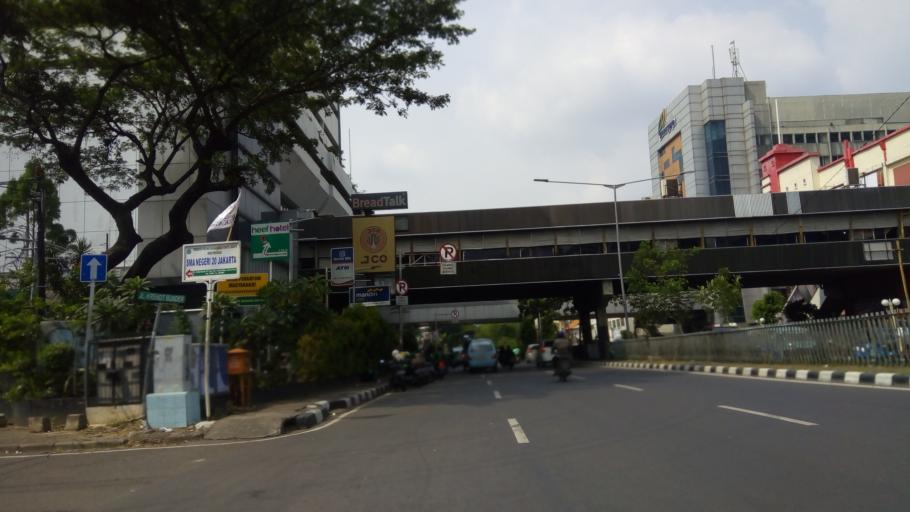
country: ID
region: Jakarta Raya
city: Jakarta
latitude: -6.1614
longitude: 106.8317
